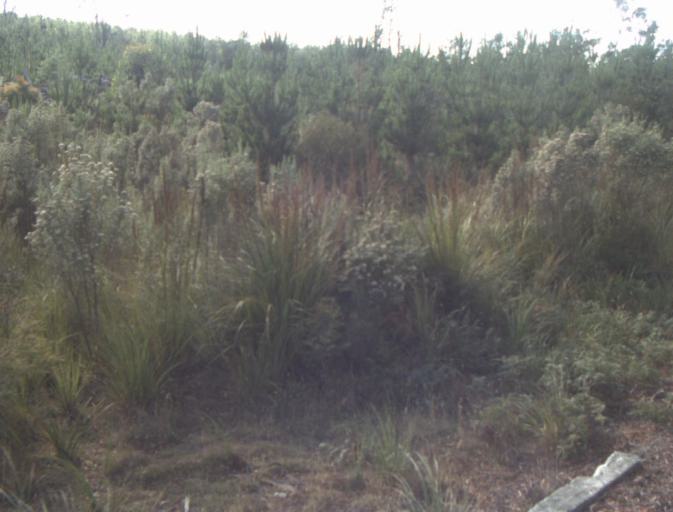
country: AU
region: Tasmania
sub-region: Dorset
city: Bridport
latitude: -41.1431
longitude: 147.2290
